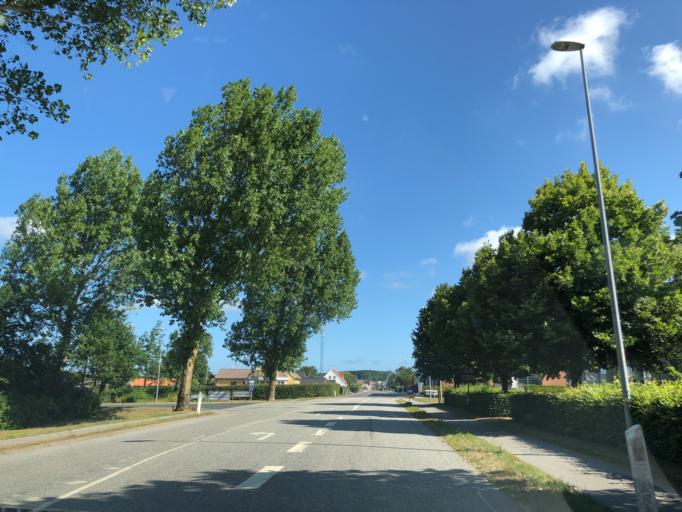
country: DK
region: North Denmark
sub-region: Jammerbugt Kommune
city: Fjerritslev
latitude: 57.0809
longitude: 9.2639
